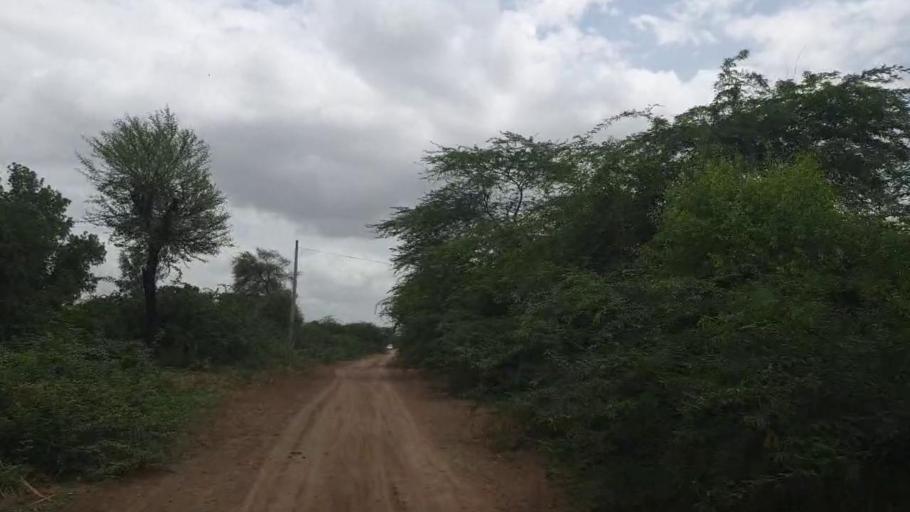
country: PK
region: Sindh
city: Badin
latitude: 24.6343
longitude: 68.9484
